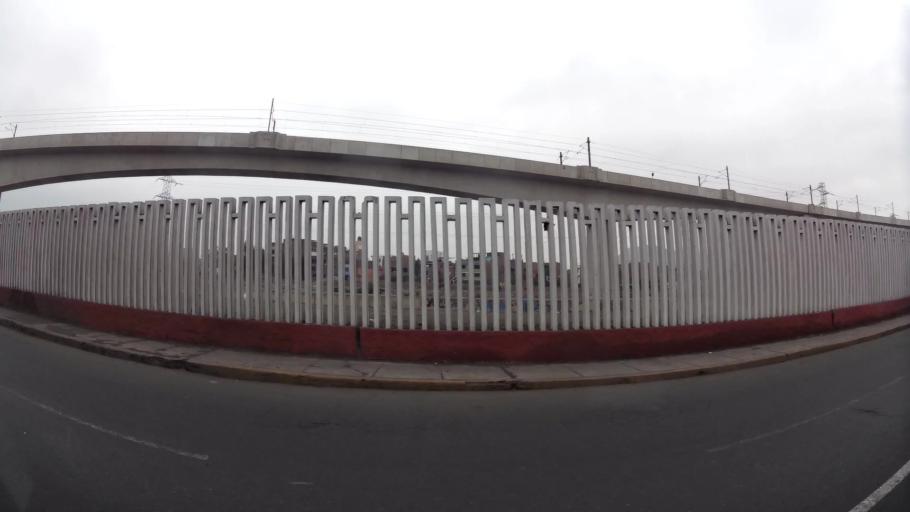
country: PE
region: Lima
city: Lima
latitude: -12.0334
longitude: -77.0124
